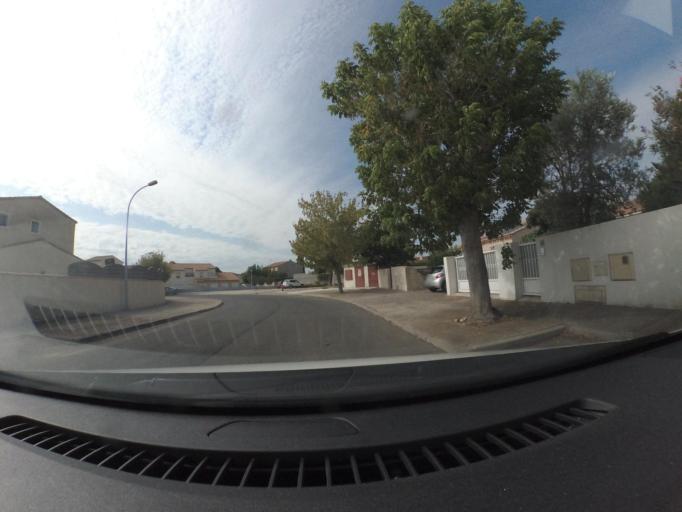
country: FR
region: Languedoc-Roussillon
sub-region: Departement de l'Herault
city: Baillargues
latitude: 43.6667
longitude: 4.0206
